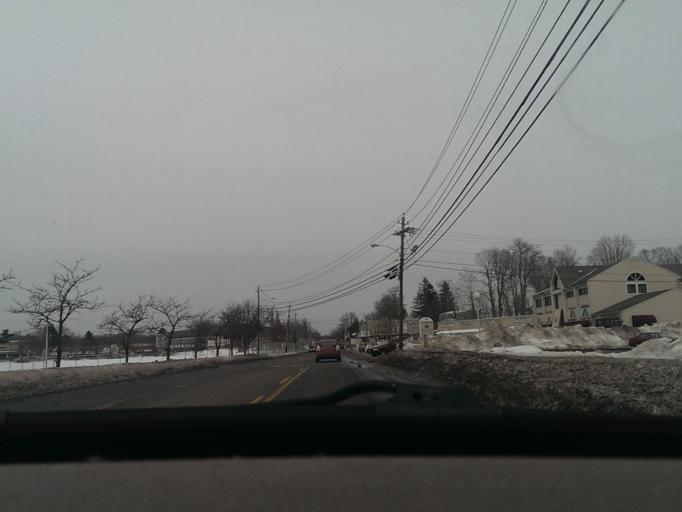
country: US
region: Massachusetts
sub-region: Hampden County
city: East Longmeadow
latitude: 42.0619
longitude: -72.5146
